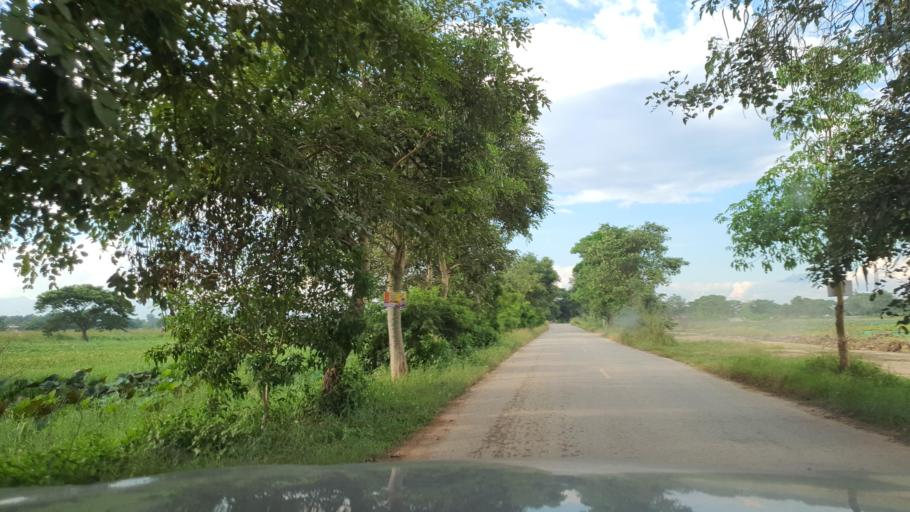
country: TH
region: Phayao
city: Phayao
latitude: 19.1961
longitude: 99.8589
